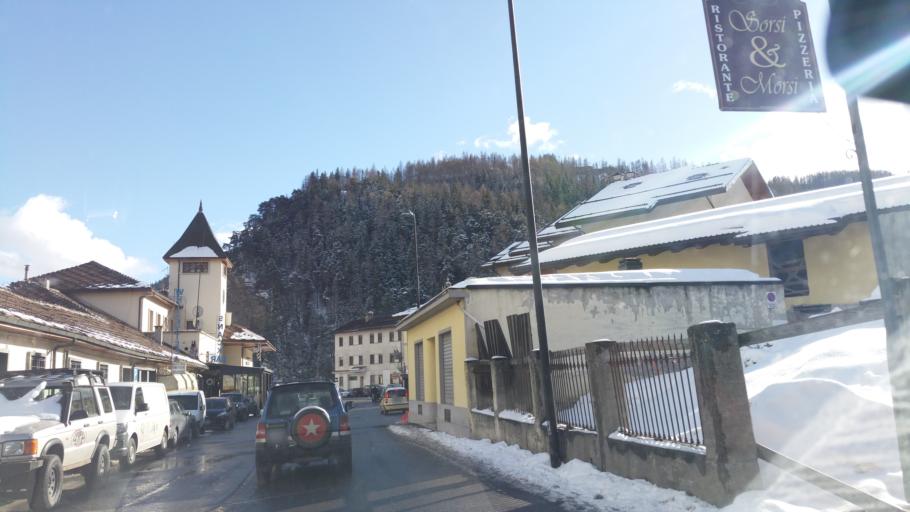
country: IT
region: Piedmont
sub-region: Provincia di Torino
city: Bardonecchia
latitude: 45.0770
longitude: 6.7093
